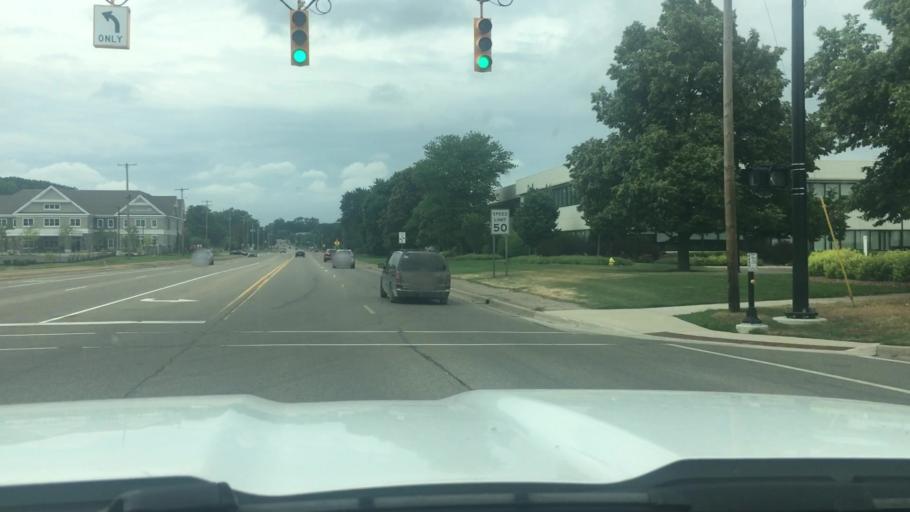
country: US
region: Michigan
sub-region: Kent County
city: Forest Hills
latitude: 42.9577
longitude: -85.4899
